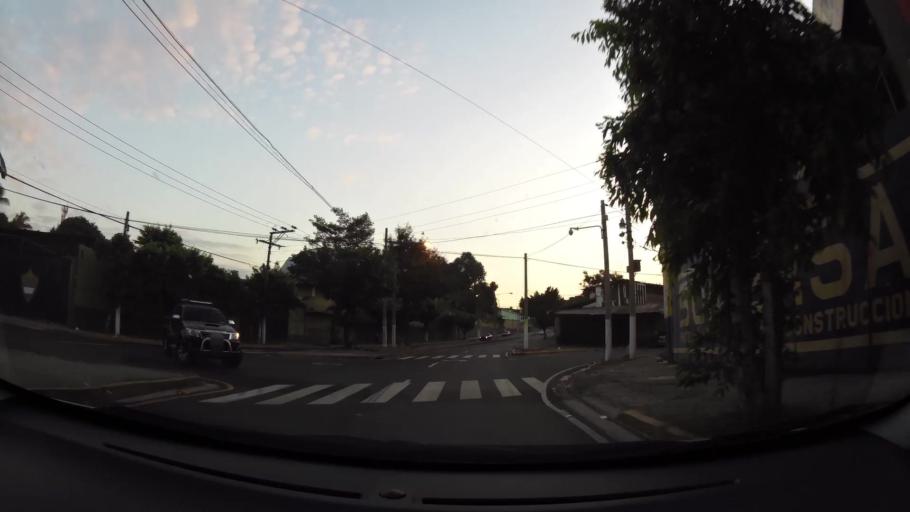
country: SV
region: San Salvador
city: Delgado
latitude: 13.7075
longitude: -89.1777
